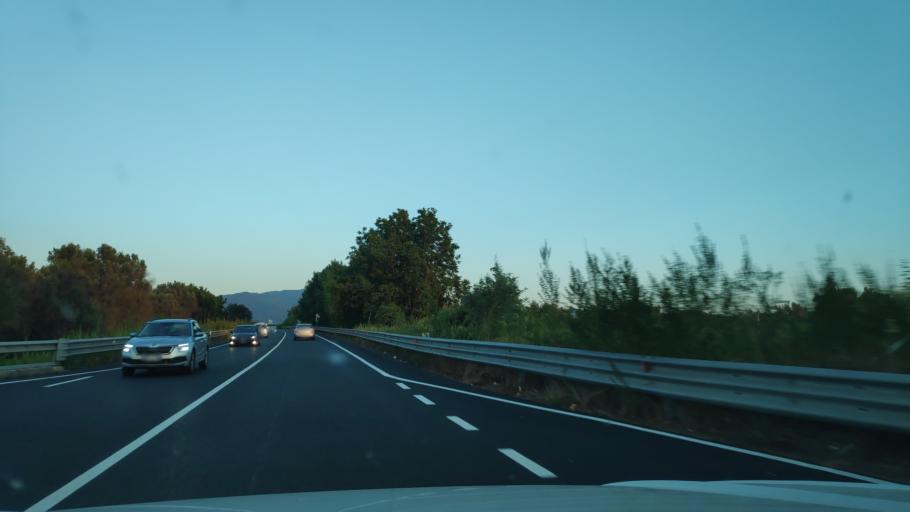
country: IT
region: Calabria
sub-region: Provincia di Reggio Calabria
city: Melicucco
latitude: 38.4209
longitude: 16.0649
